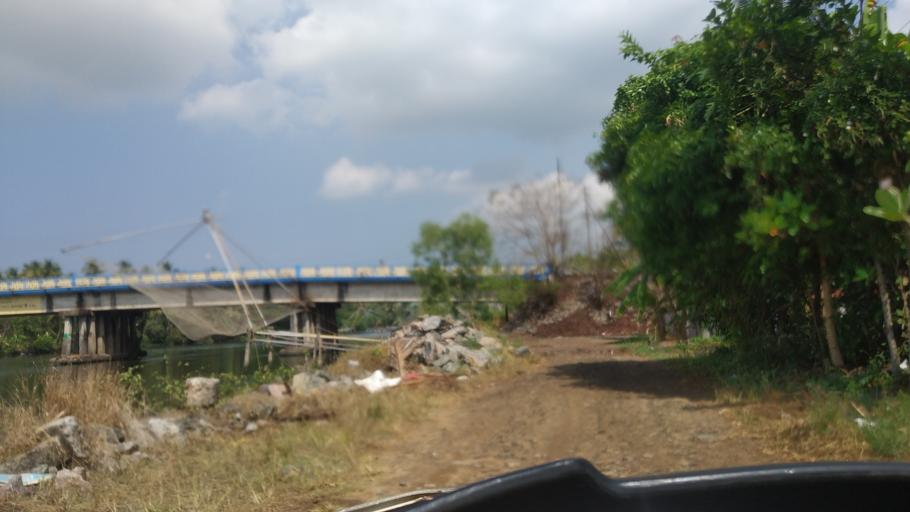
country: IN
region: Kerala
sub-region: Thrissur District
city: Kodungallur
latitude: 10.1400
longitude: 76.2026
